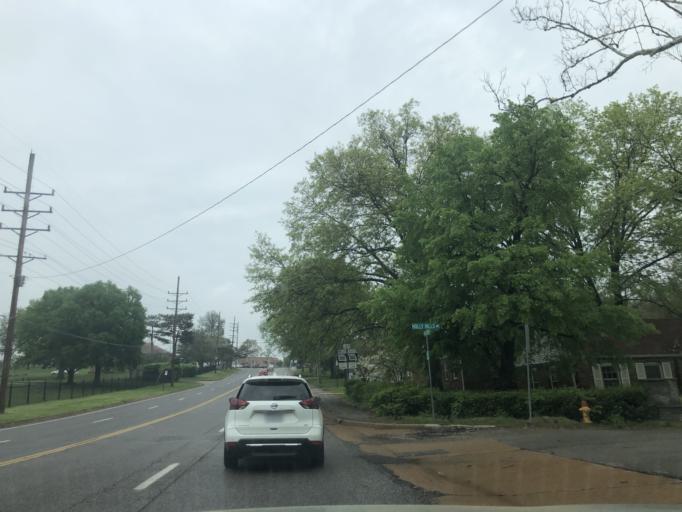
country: US
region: Missouri
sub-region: Saint Louis County
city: Shrewsbury
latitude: 38.5805
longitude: -90.3185
